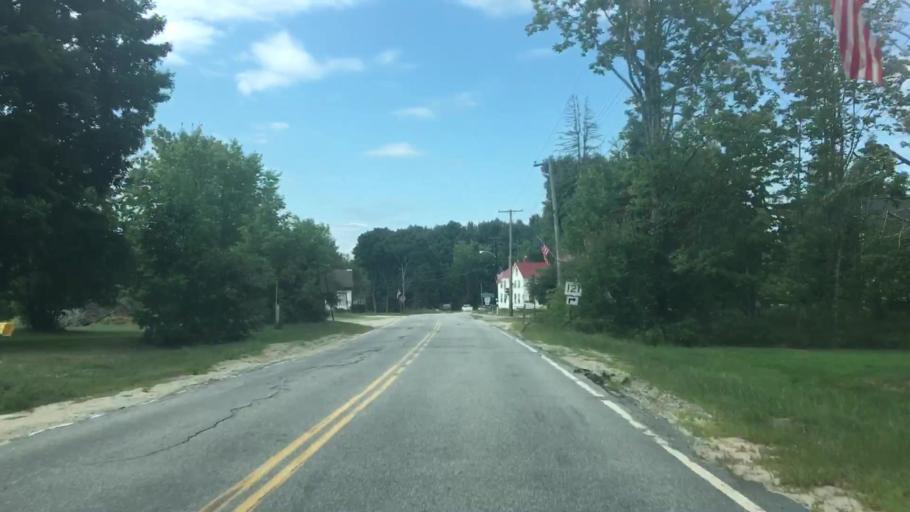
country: US
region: Maine
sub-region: Oxford County
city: Oxford
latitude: 44.0560
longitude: -70.5550
